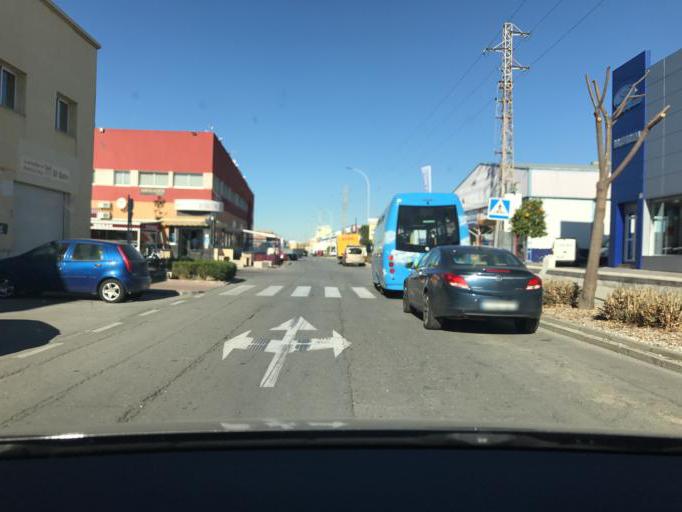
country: ES
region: Andalusia
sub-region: Provincia de Granada
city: Peligros
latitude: 37.2229
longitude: -3.6368
